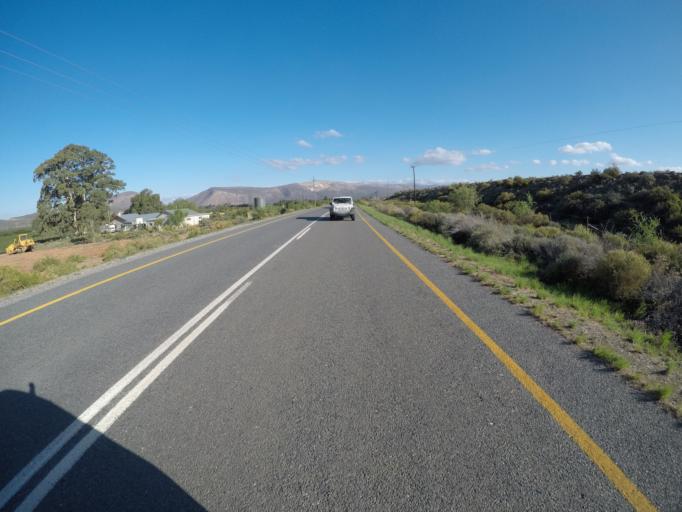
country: ZA
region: Western Cape
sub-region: Cape Winelands District Municipality
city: Ashton
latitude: -33.7944
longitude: 19.7805
